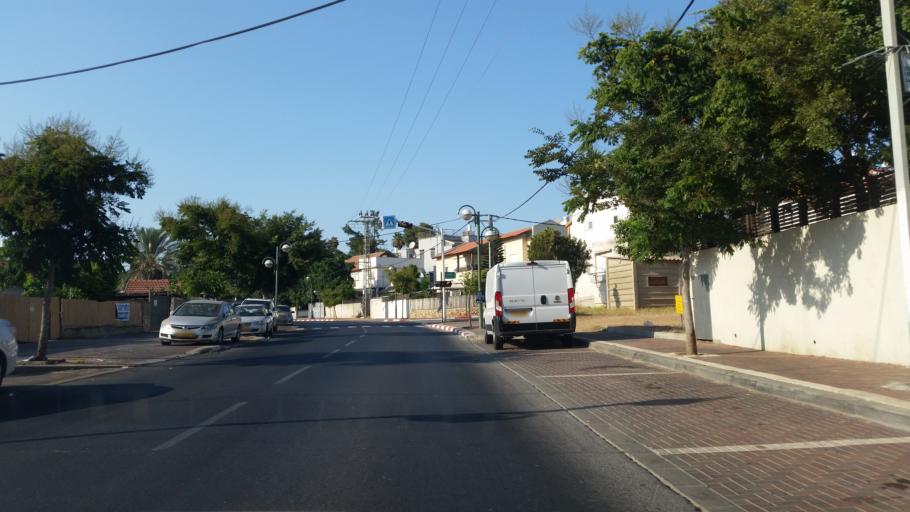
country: IL
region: Tel Aviv
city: Ramat HaSharon
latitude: 32.1336
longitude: 34.8525
